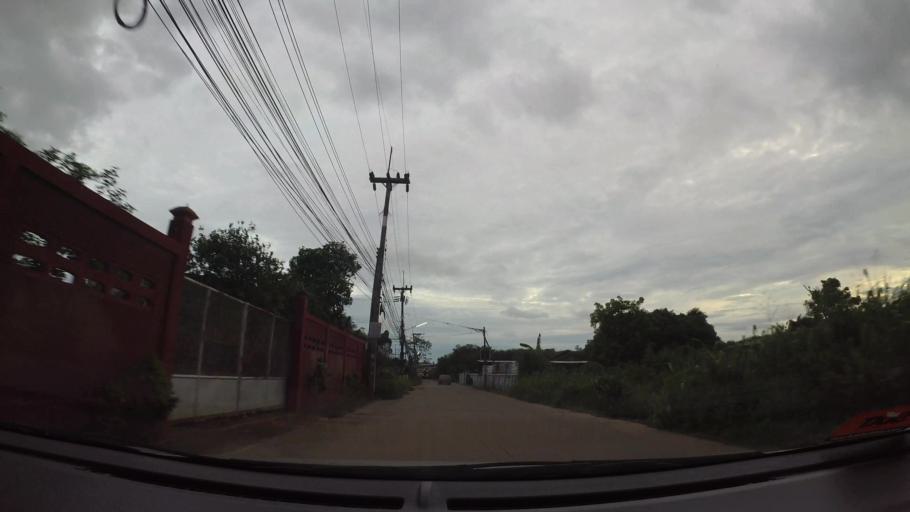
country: TH
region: Chon Buri
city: Sattahip
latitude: 12.6953
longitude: 100.8947
